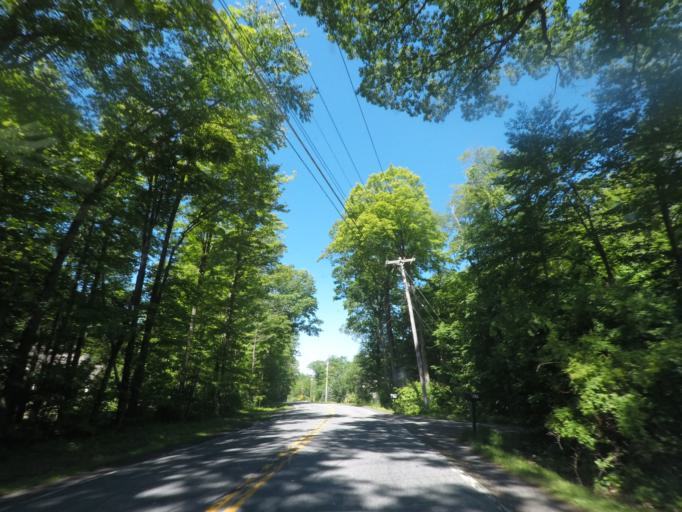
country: US
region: New York
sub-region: Saratoga County
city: Country Knolls
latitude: 42.8742
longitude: -73.8581
